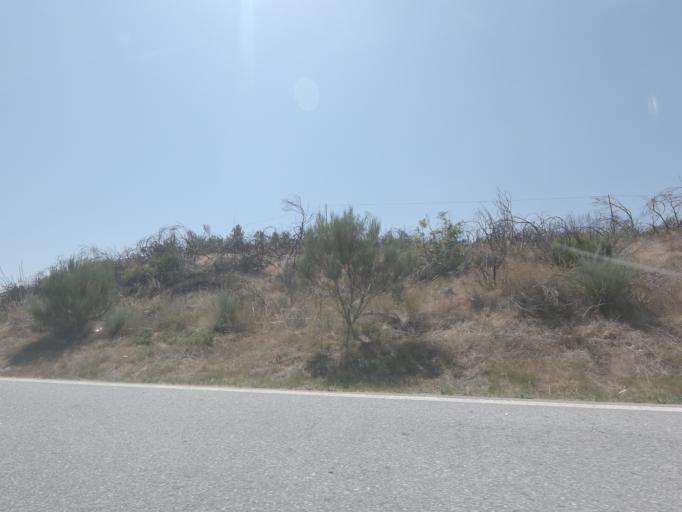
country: PT
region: Viseu
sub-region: Castro Daire
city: Castro Daire
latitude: 40.9706
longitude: -7.8839
